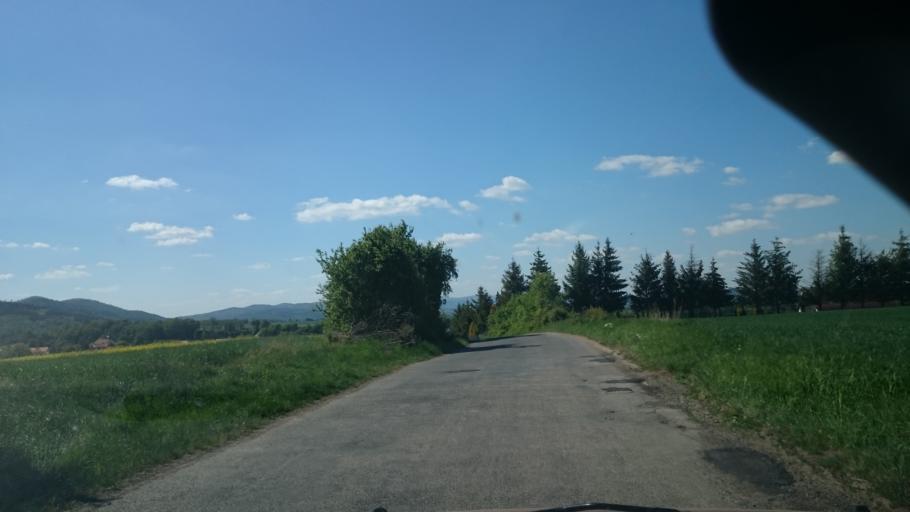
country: PL
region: Lower Silesian Voivodeship
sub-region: Powiat zabkowicki
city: Kamieniec Zabkowicki
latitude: 50.4885
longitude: 16.8342
